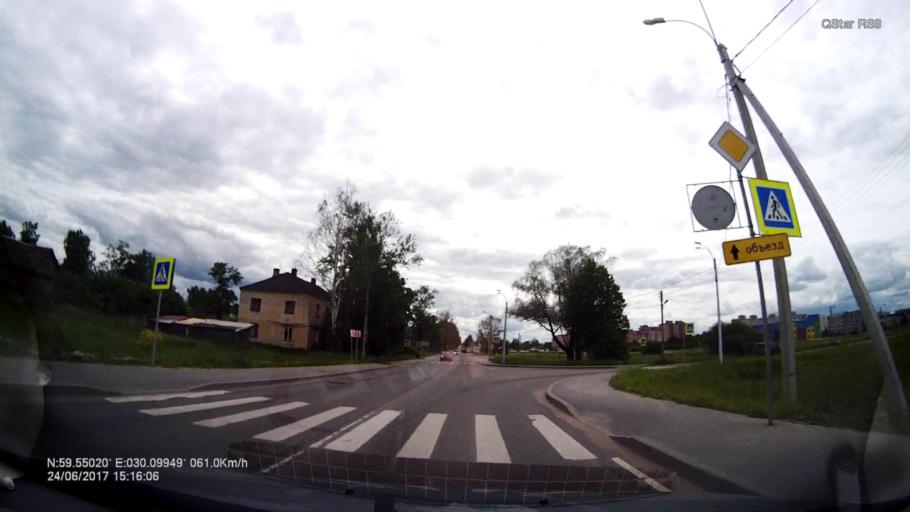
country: RU
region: Leningrad
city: Gatchina
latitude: 59.5502
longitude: 30.0995
